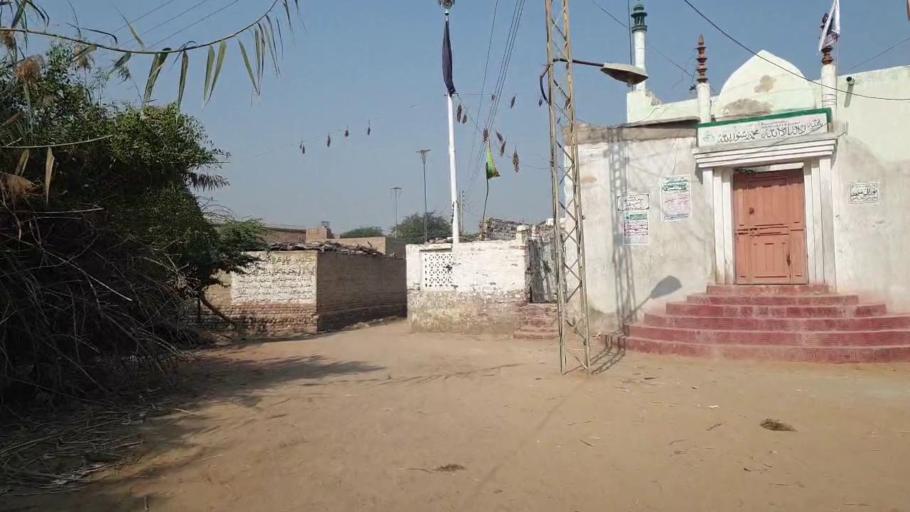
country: PK
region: Sindh
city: Kotri
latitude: 25.3507
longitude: 68.3083
